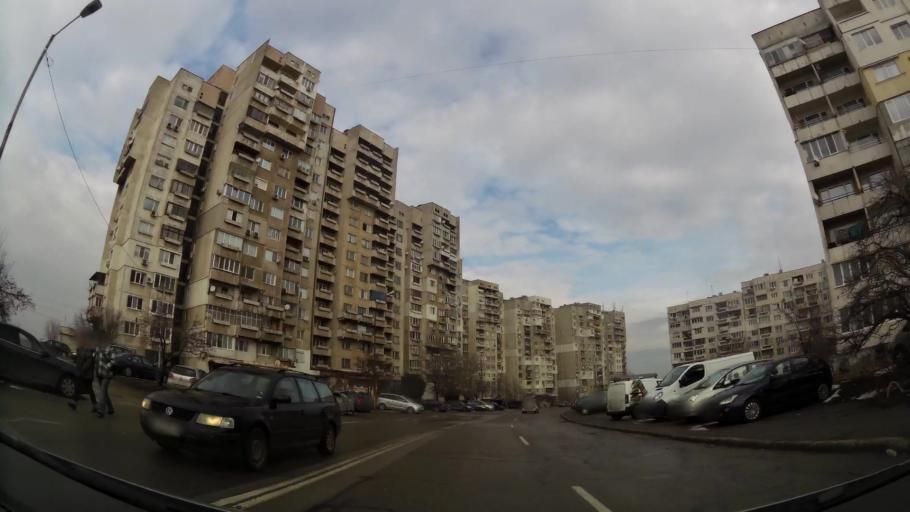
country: BG
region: Sofiya
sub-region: Obshtina Bozhurishte
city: Bozhurishte
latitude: 42.7149
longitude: 23.2368
